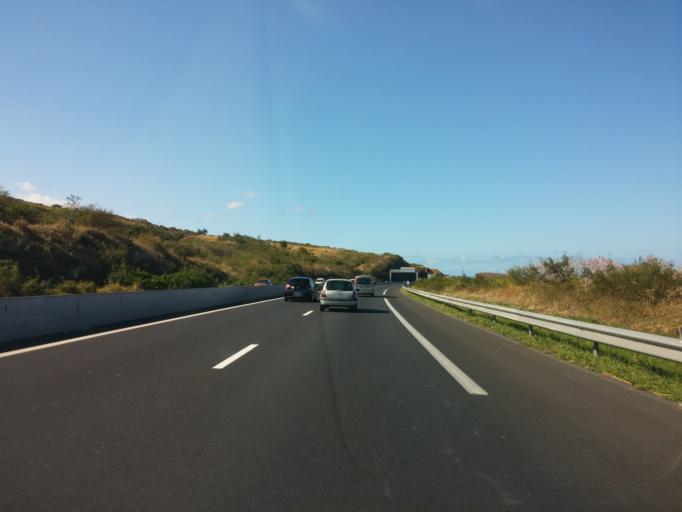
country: RE
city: Piton Saint-Leu
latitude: -21.2310
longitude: 55.3108
